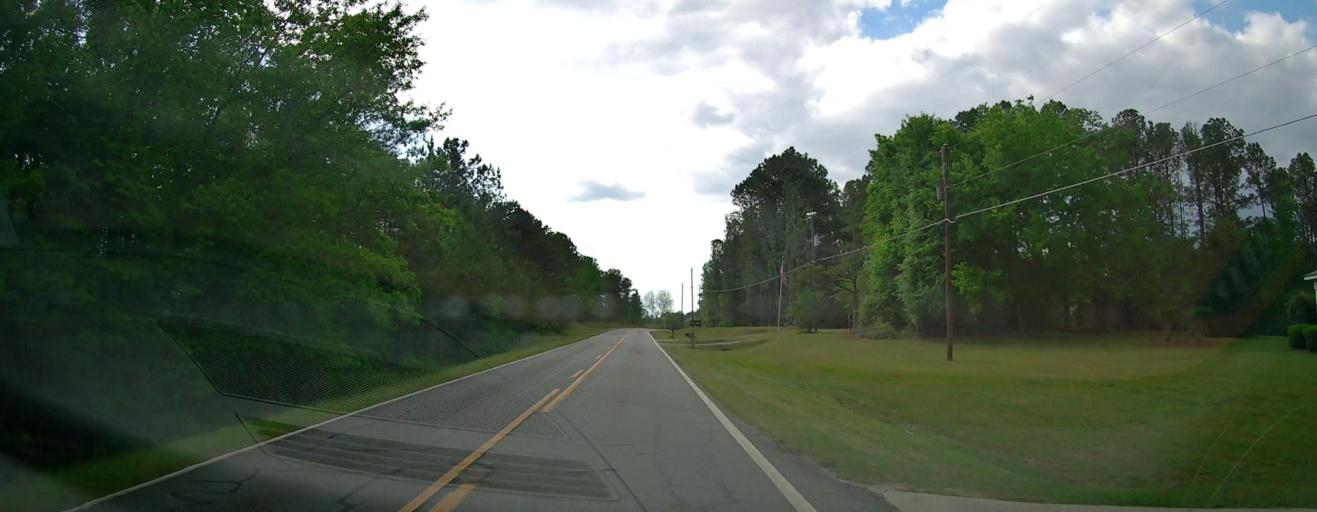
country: US
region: Georgia
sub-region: Baldwin County
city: Hardwick
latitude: 33.0650
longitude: -83.1704
